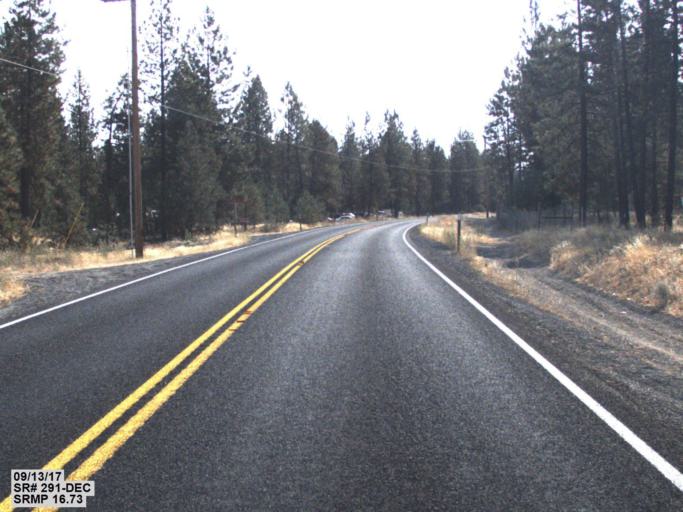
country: US
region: Washington
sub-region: Spokane County
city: Deer Park
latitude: 47.8437
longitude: -117.6214
